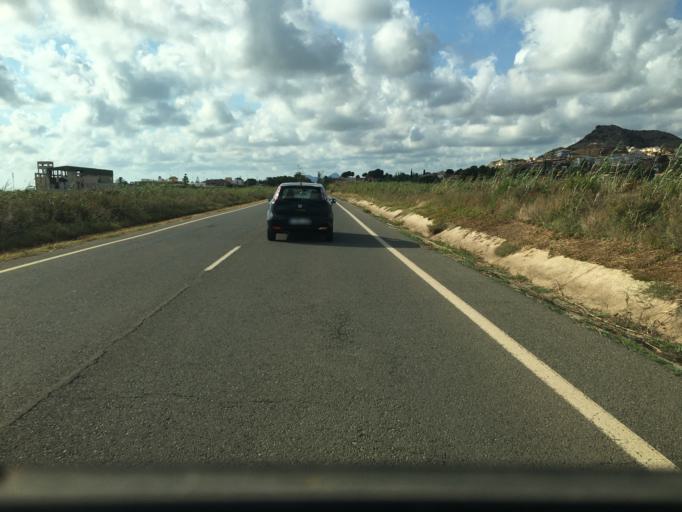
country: ES
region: Murcia
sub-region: Murcia
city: Los Alcazares
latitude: 37.6985
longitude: -0.8446
